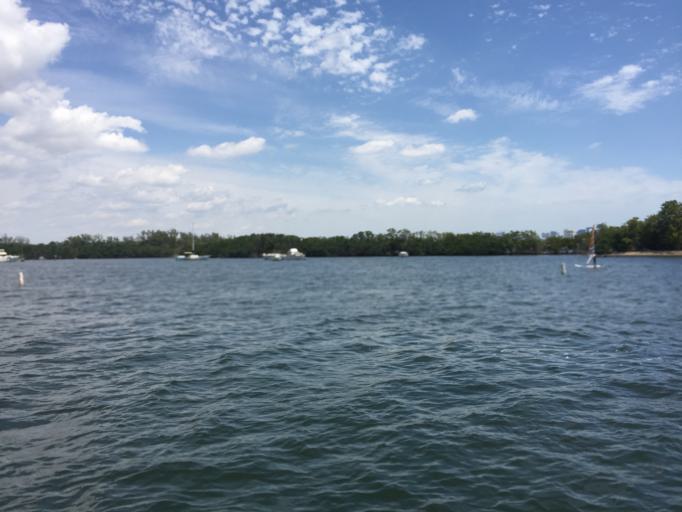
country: US
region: Florida
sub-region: Miami-Dade County
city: Coconut Grove
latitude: 25.7288
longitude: -80.2285
